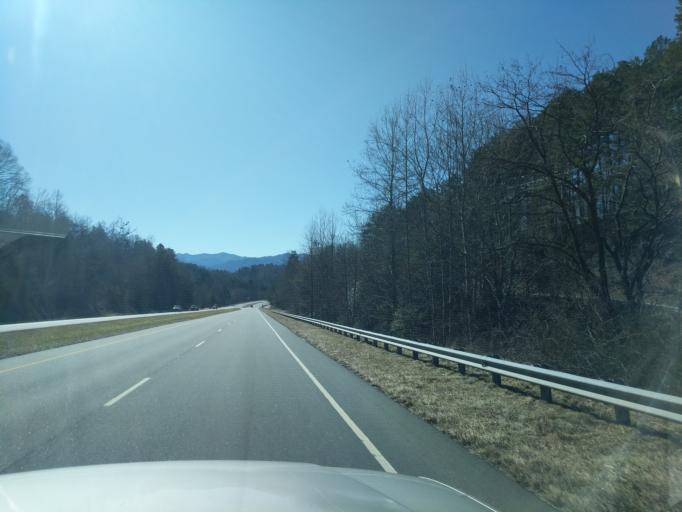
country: US
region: North Carolina
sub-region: Swain County
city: Bryson City
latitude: 35.3792
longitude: -83.4989
